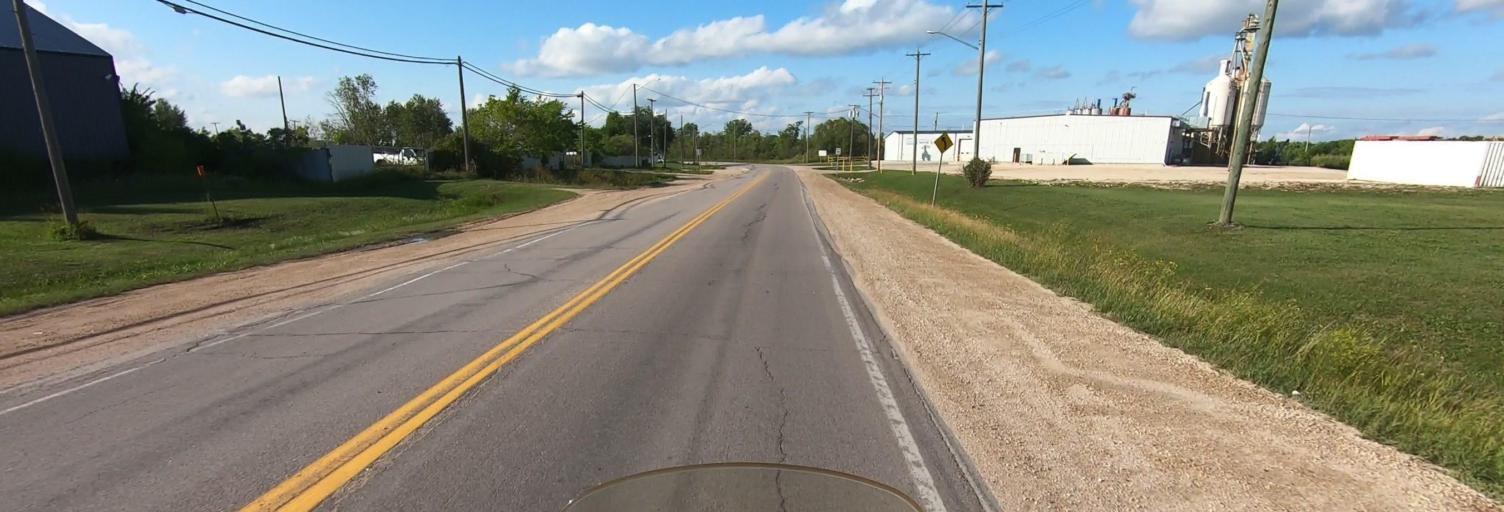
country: CA
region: Manitoba
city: Selkirk
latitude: 50.1534
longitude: -96.8667
